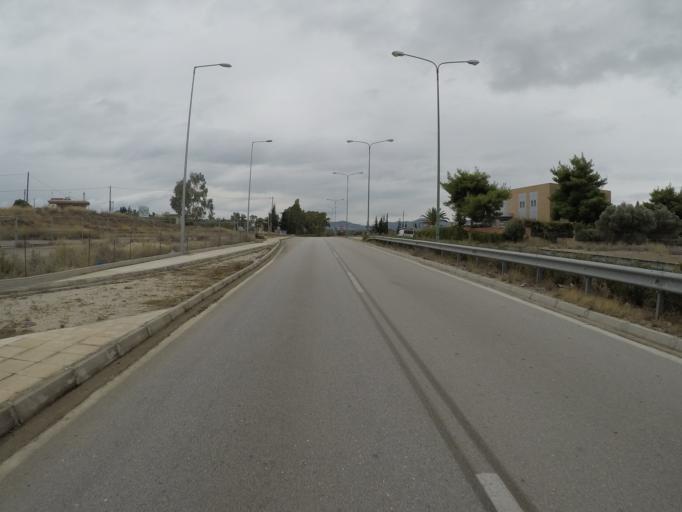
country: GR
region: Peloponnese
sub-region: Nomos Korinthias
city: Korinthos
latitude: 37.9430
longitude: 22.9791
